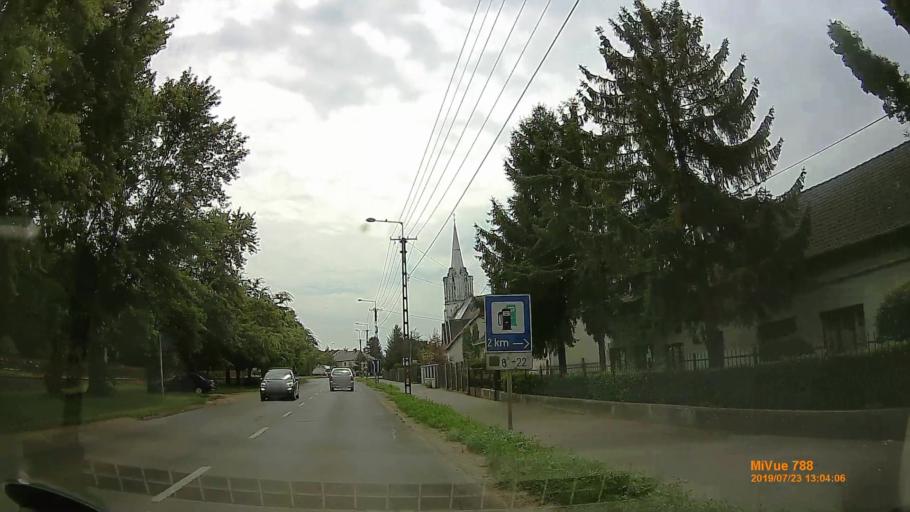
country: HU
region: Szabolcs-Szatmar-Bereg
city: Tiszavasvari
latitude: 47.9527
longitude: 21.3692
